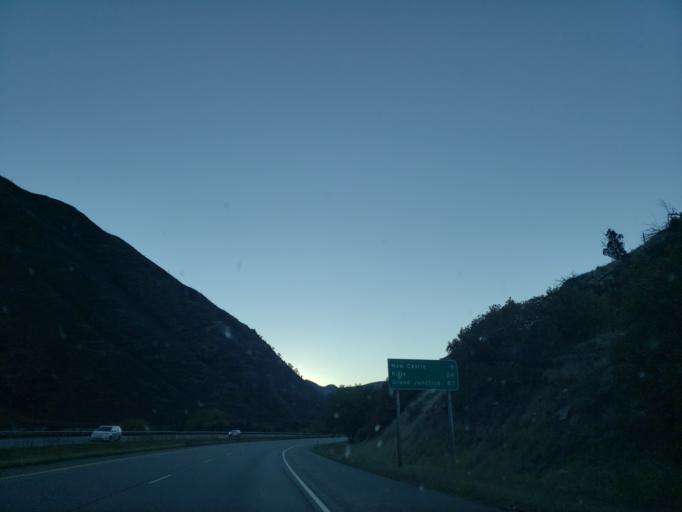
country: US
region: Colorado
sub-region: Garfield County
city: Glenwood Springs
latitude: 39.5609
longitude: -107.3742
